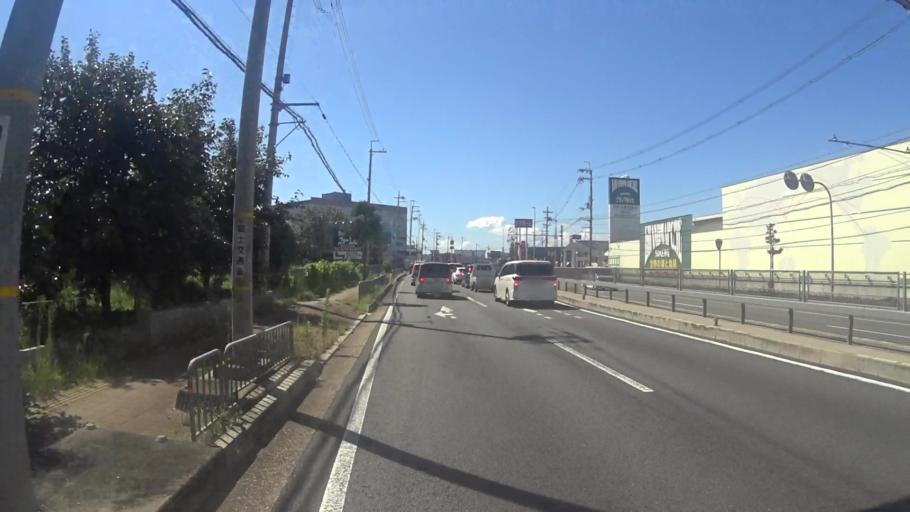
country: JP
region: Kyoto
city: Yawata
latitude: 34.8919
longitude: 135.7439
